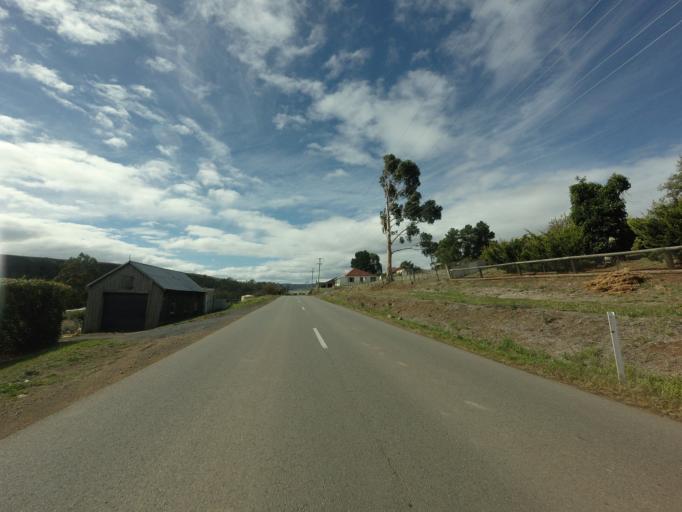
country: AU
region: Tasmania
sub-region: Derwent Valley
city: New Norfolk
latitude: -42.7000
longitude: 146.9184
